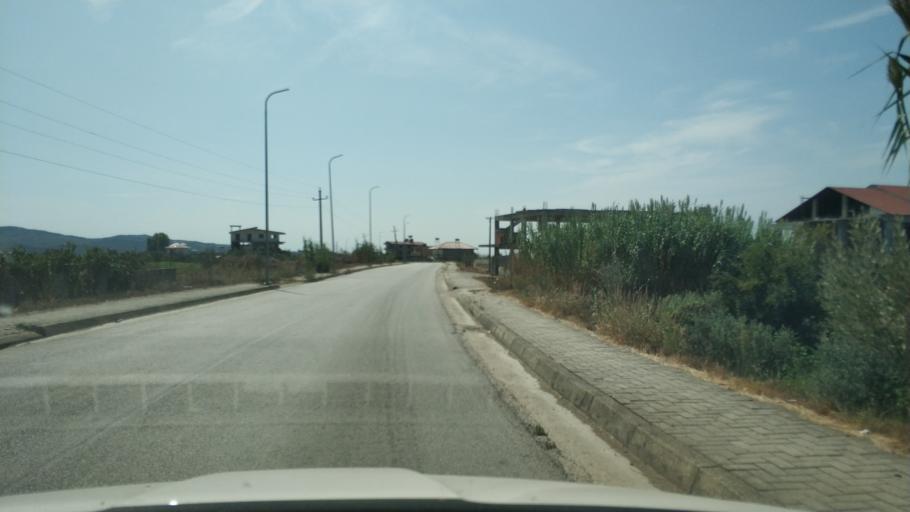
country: AL
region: Fier
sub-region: Rrethi i Lushnjes
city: Divjake
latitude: 40.9862
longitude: 19.5346
